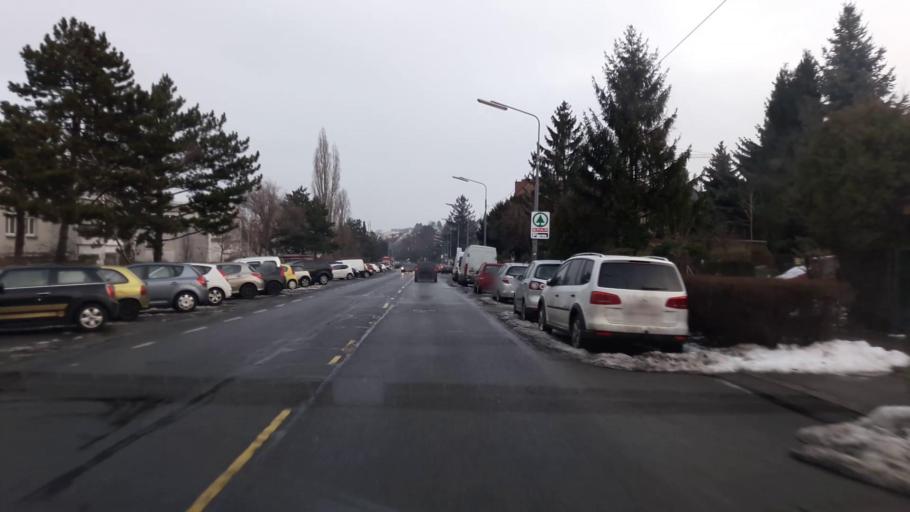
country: AT
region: Lower Austria
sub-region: Politischer Bezirk Wien-Umgebung
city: Klosterneuburg
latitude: 48.2444
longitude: 16.3191
